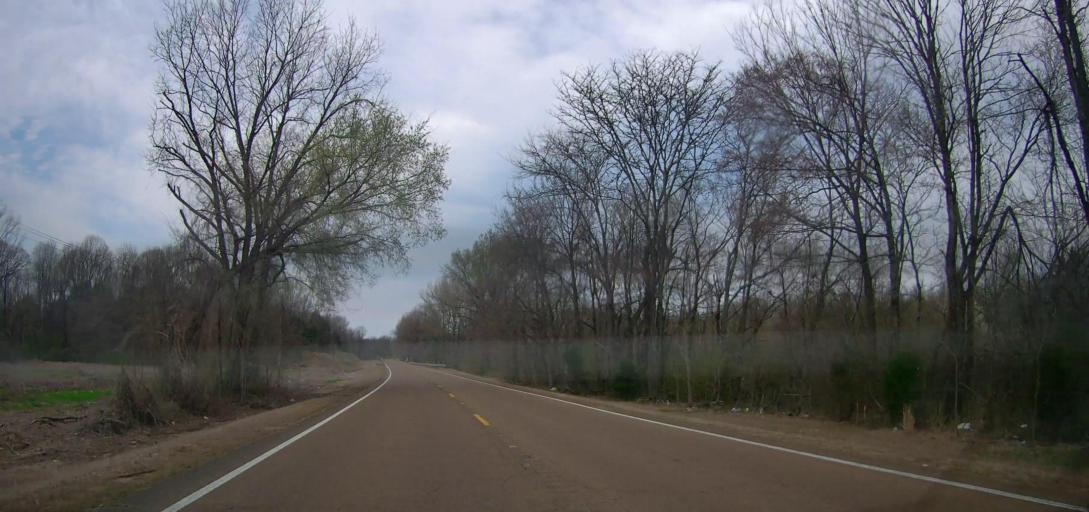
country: US
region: Mississippi
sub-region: Marshall County
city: Byhalia
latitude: 34.8471
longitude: -89.6206
